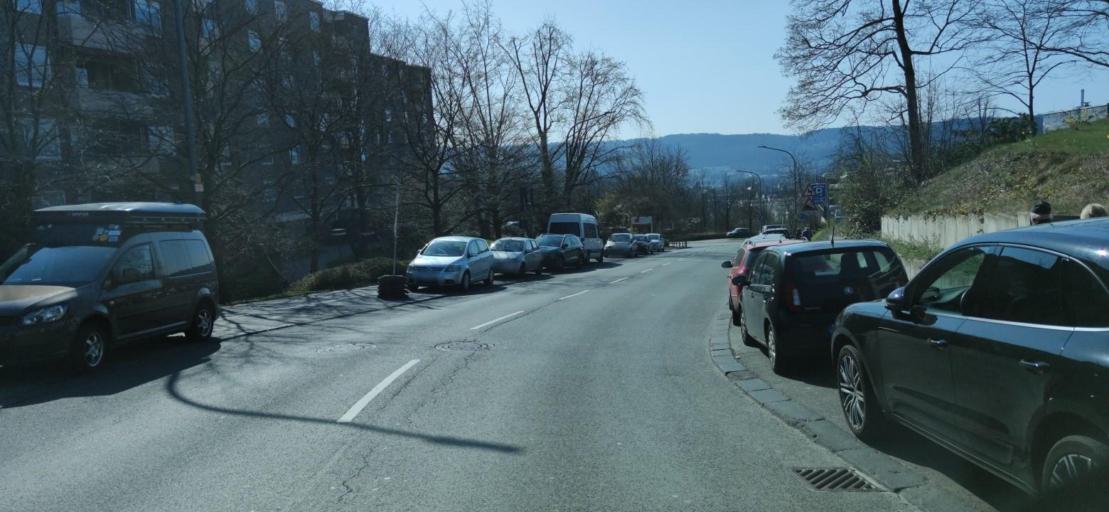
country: DE
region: North Rhine-Westphalia
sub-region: Regierungsbezirk Dusseldorf
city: Wuppertal
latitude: 51.2676
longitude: 7.1313
